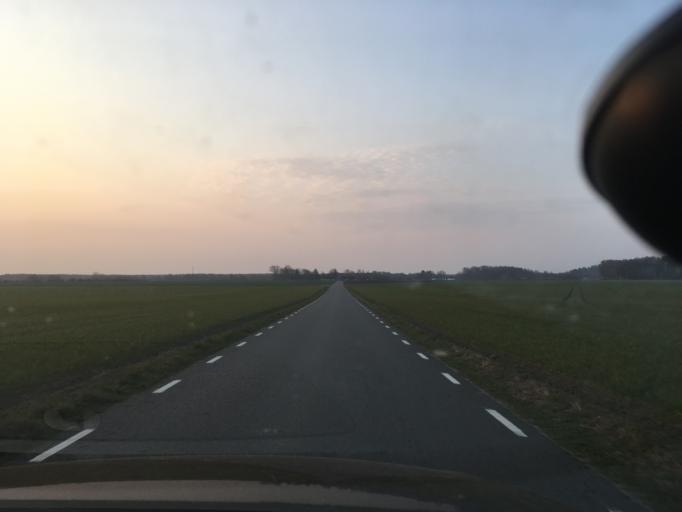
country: SE
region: Skane
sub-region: Ystads Kommun
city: Kopingebro
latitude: 55.4076
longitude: 14.1564
